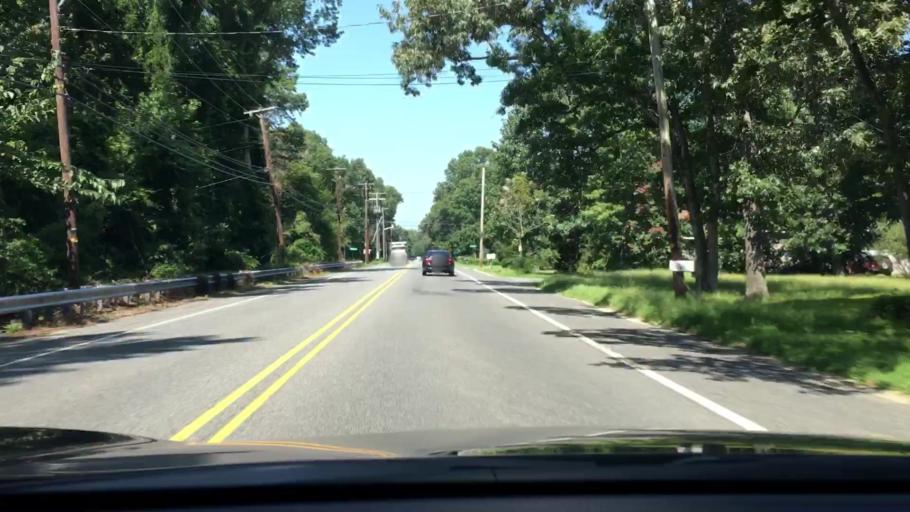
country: US
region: New Jersey
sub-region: Cumberland County
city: Laurel Lake
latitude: 39.3377
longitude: -75.0266
